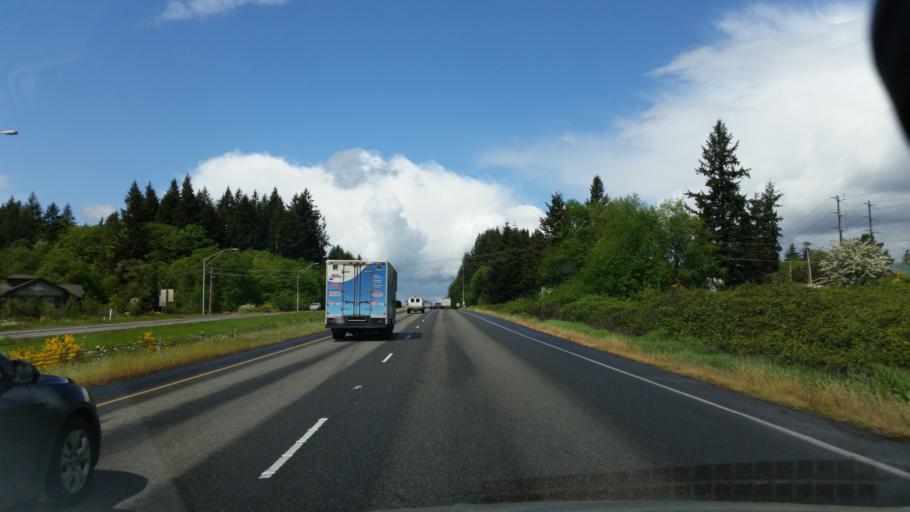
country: US
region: Washington
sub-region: Pierce County
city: Gig Harbor
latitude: 47.3221
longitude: -122.5911
